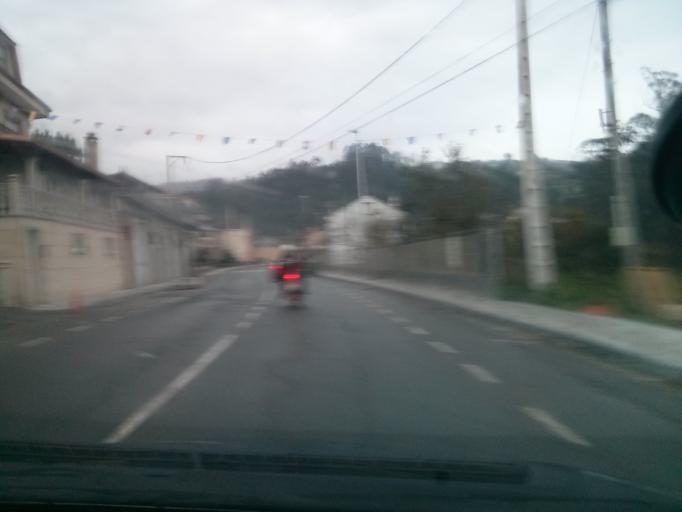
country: ES
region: Galicia
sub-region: Provincia da Coruna
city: Outes
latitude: 42.8325
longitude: -8.8751
